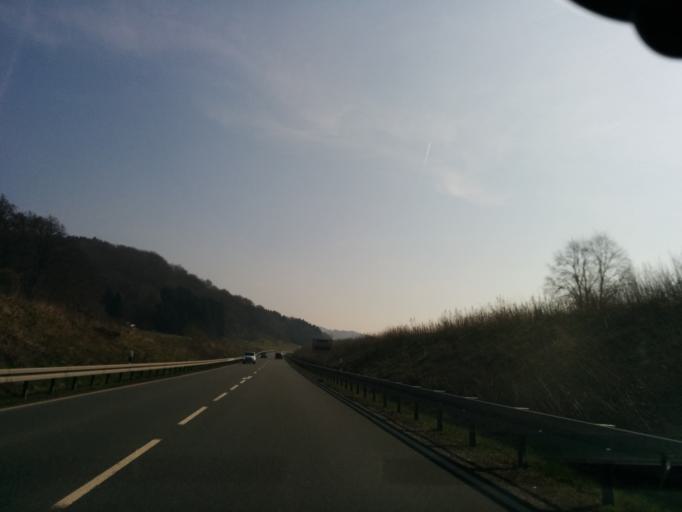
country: DE
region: Lower Saxony
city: Bad Lauterberg im Harz
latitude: 51.6249
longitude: 10.4374
